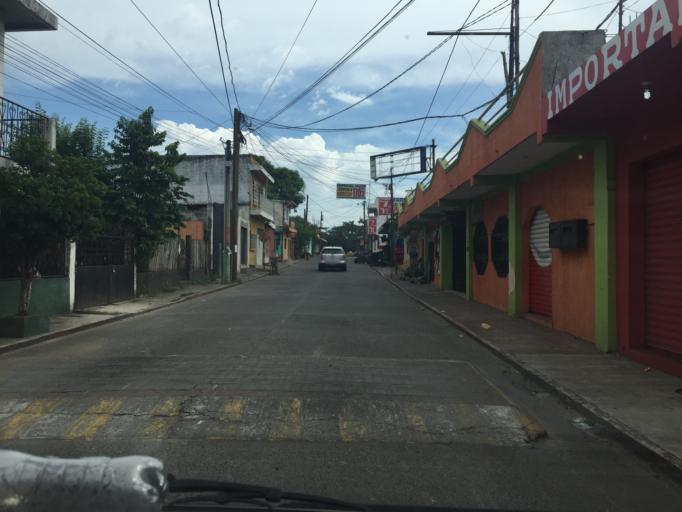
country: GT
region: Suchitepeque
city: Patulul
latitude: 14.4212
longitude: -91.1630
